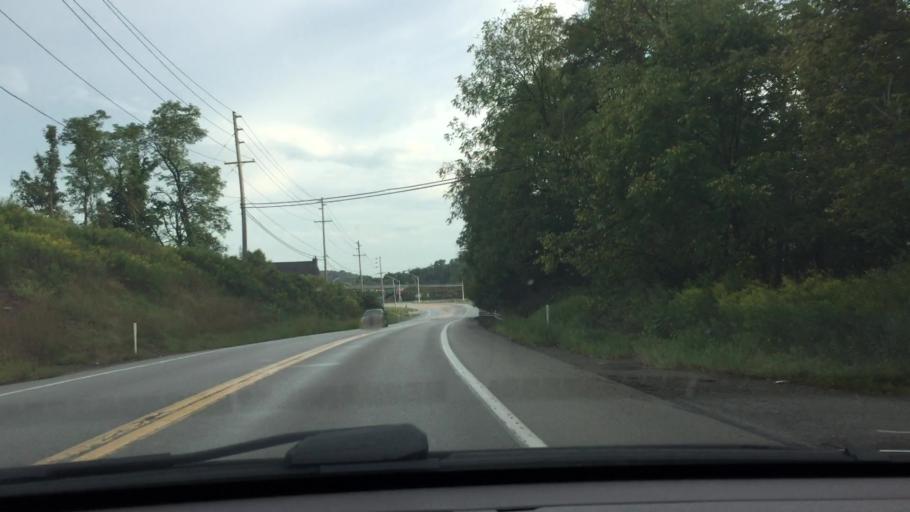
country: US
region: Pennsylvania
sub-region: Washington County
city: East Washington
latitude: 40.1599
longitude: -80.1322
